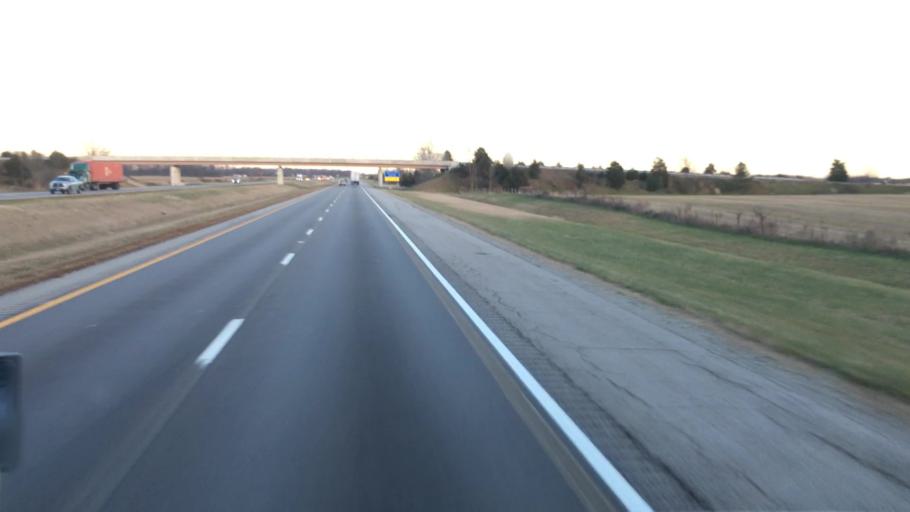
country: US
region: Ohio
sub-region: Montgomery County
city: Brookville
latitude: 39.8379
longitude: -84.4663
